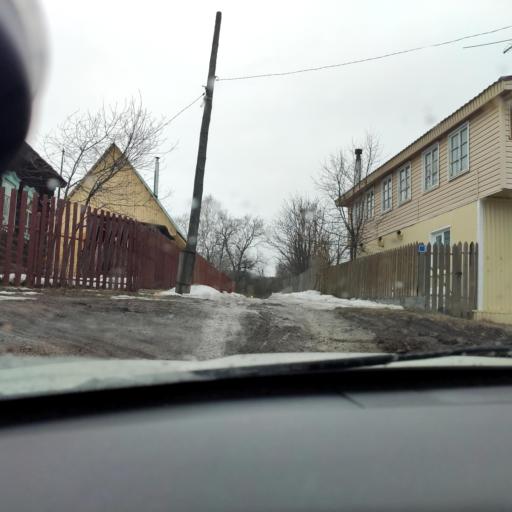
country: RU
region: Perm
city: Lobanovo
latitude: 57.8536
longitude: 56.3480
